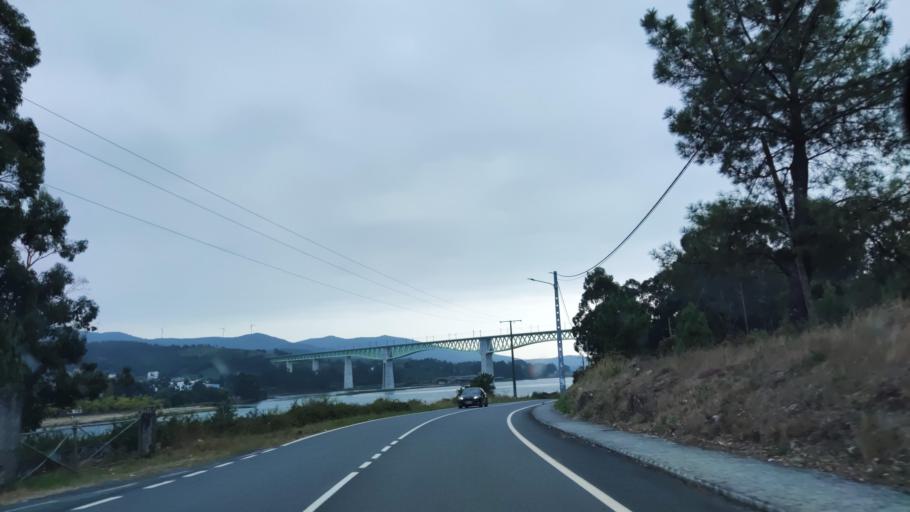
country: ES
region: Galicia
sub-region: Provincia de Pontevedra
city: Catoira
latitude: 42.6750
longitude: -8.7301
